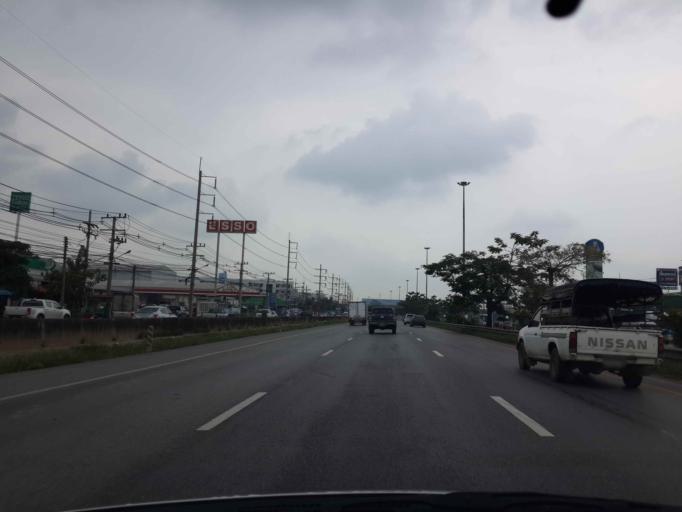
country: TH
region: Samut Sakhon
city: Samut Sakhon
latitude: 13.5432
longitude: 100.2441
